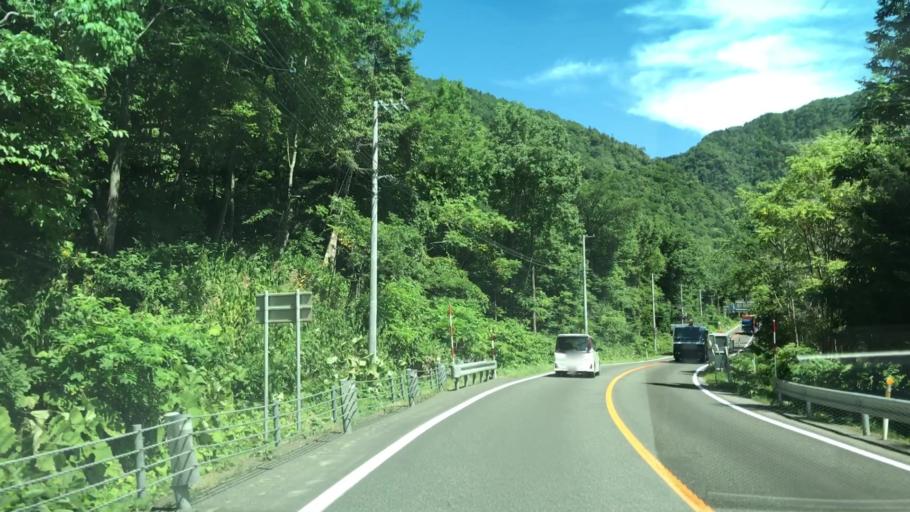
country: JP
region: Hokkaido
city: Shimo-furano
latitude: 42.9307
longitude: 142.5935
